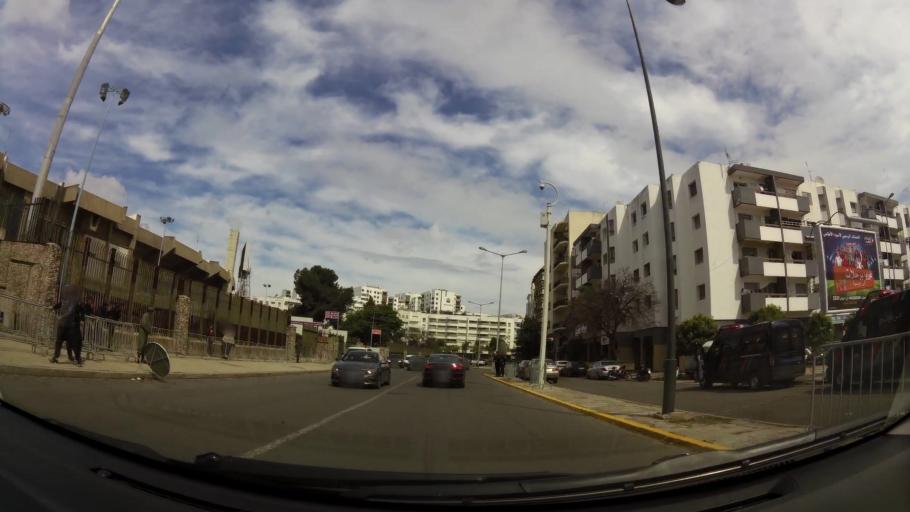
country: MA
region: Grand Casablanca
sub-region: Casablanca
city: Casablanca
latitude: 33.5834
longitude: -7.6450
